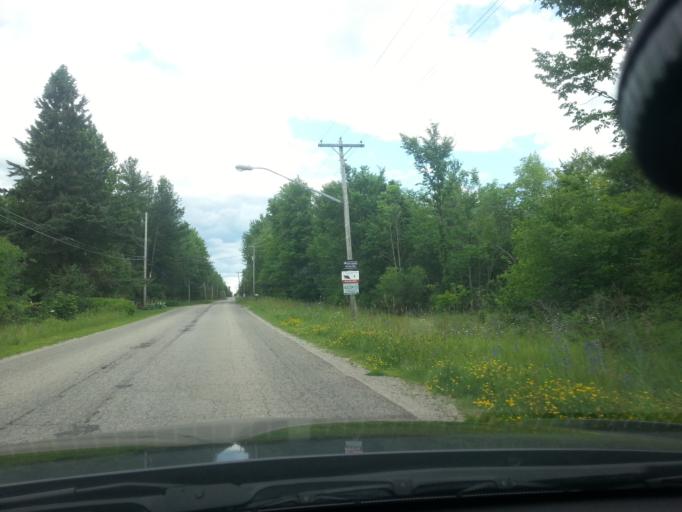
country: CA
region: Ontario
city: Gananoque
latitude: 44.6020
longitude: -76.2299
